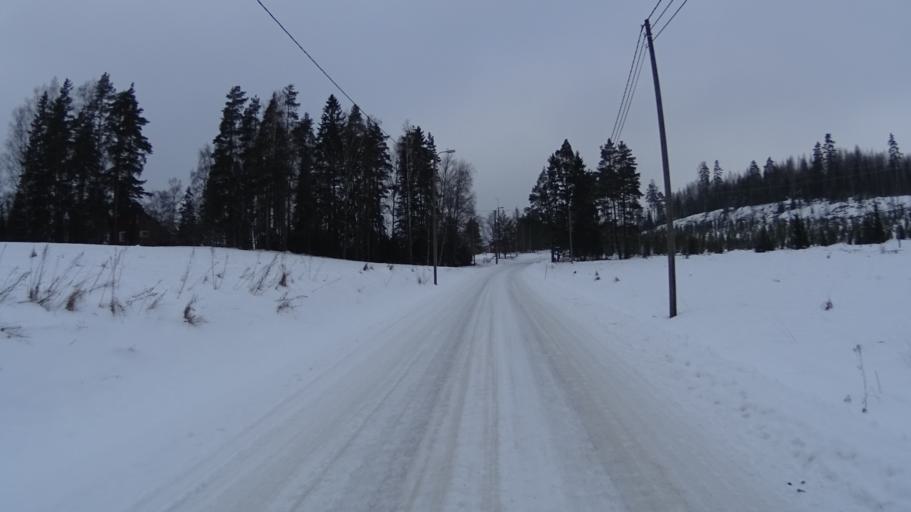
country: FI
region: Uusimaa
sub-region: Helsinki
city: Saukkola
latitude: 60.3750
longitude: 24.1060
